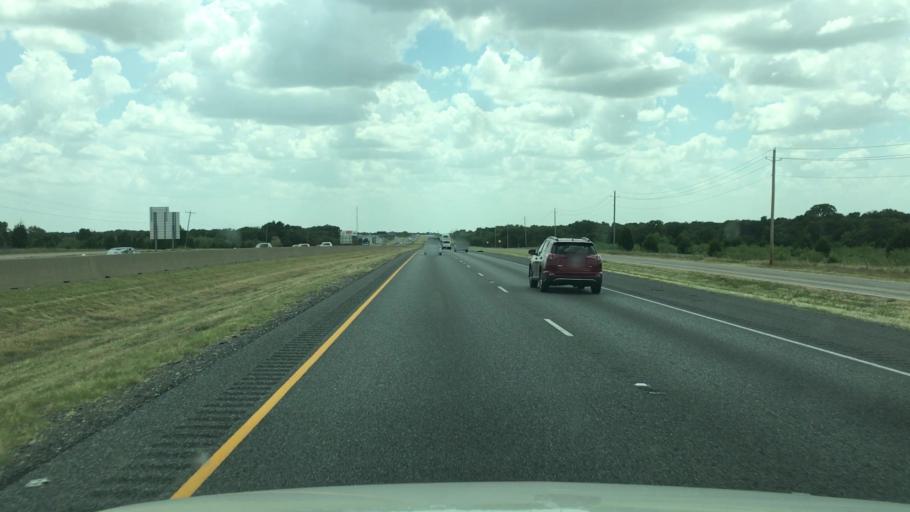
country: US
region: Texas
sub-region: Hunt County
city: Greenville
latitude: 33.0779
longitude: -96.1383
